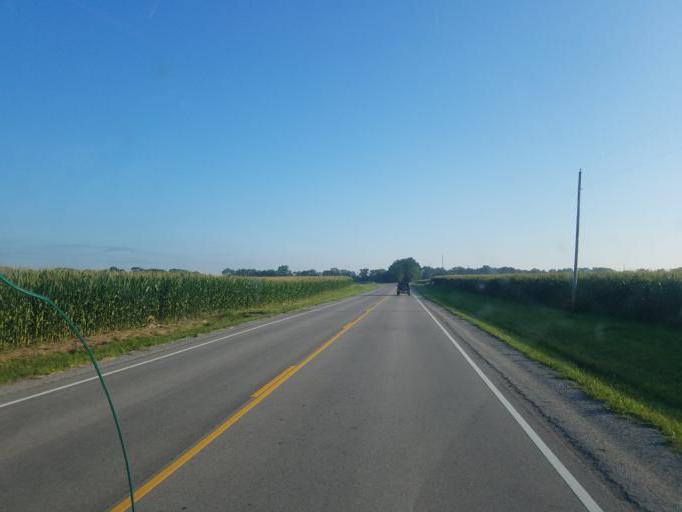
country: US
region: Illinois
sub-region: Bond County
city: Greenville
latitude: 38.8560
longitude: -89.3714
